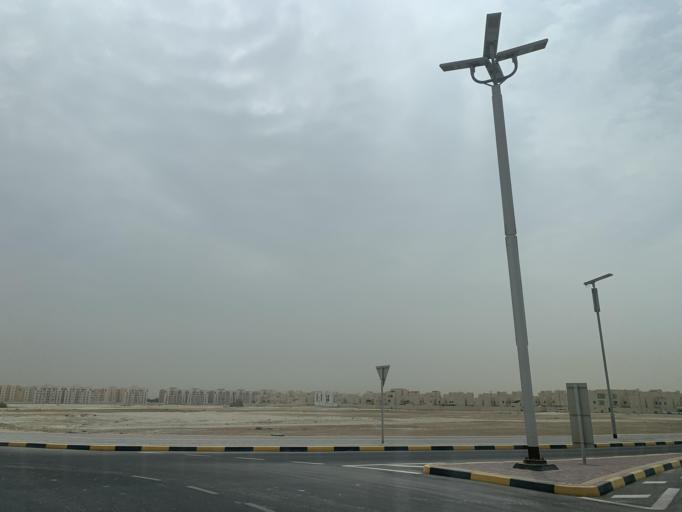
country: BH
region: Northern
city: Madinat `Isa
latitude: 26.1755
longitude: 50.5130
